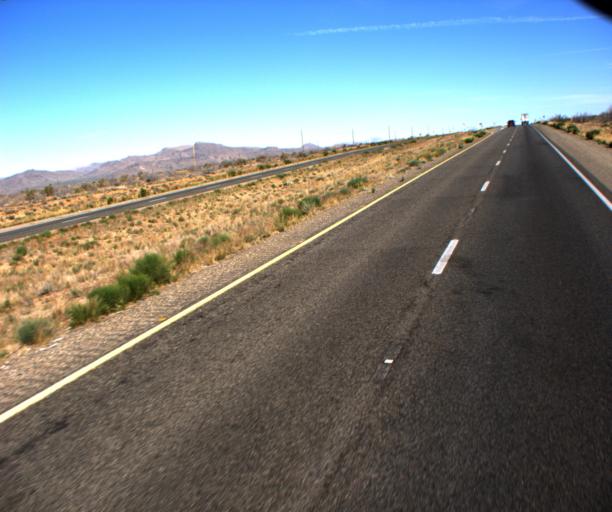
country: US
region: Arizona
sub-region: Mohave County
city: Golden Valley
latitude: 35.3070
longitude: -114.1941
